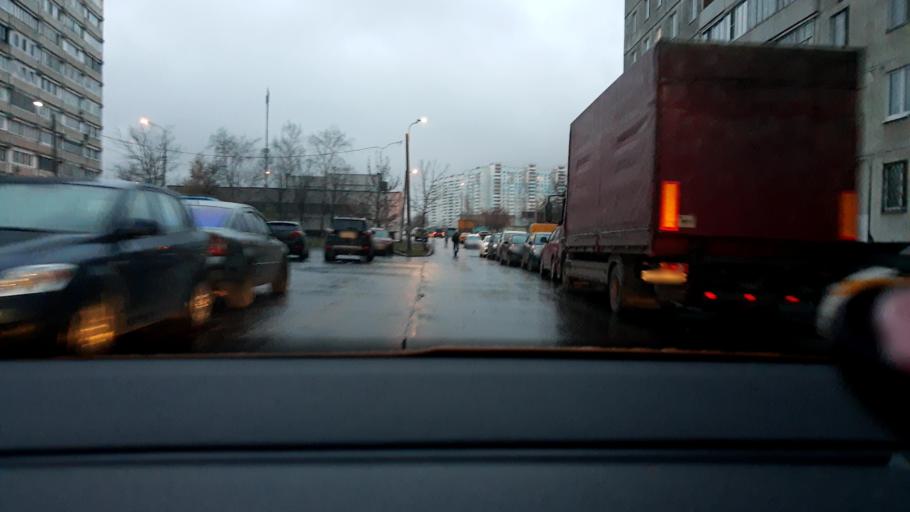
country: RU
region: Moscow
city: Bibirevo
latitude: 55.8808
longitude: 37.5919
